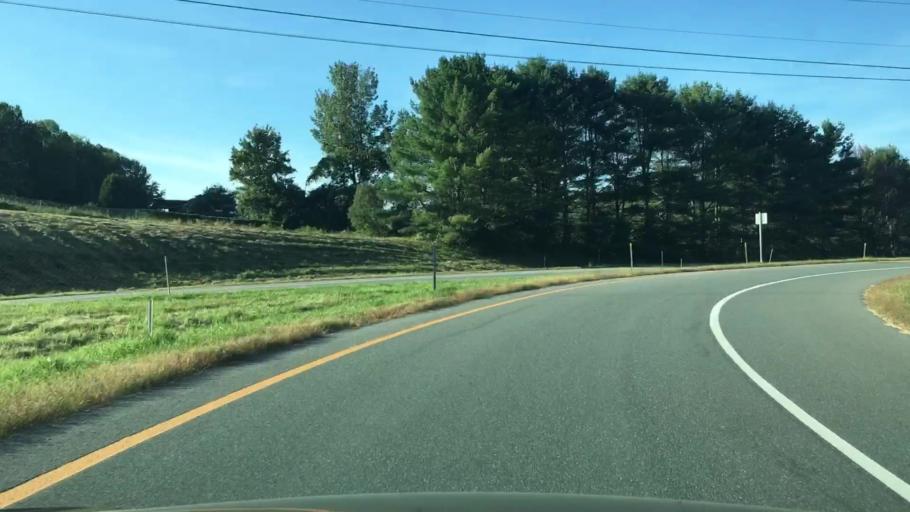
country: US
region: New Hampshire
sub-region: Grafton County
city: Littleton
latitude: 44.3259
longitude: -71.8082
